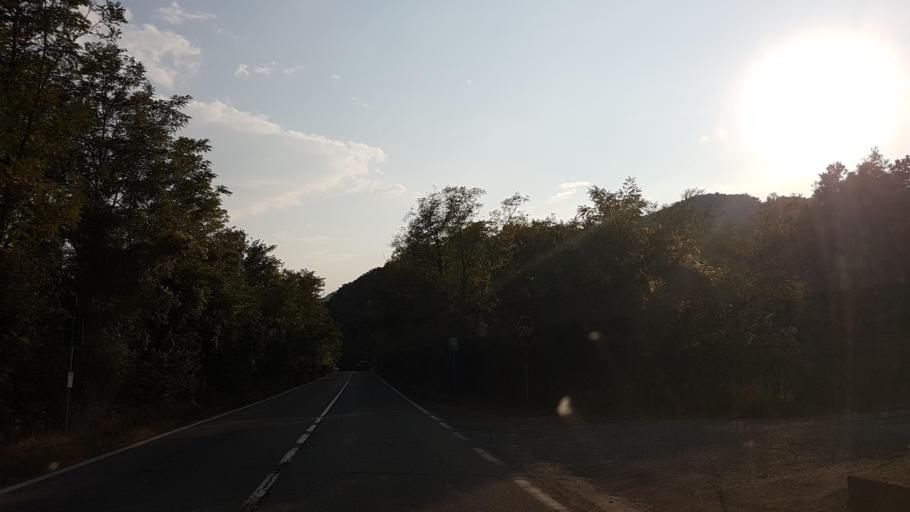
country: IT
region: Emilia-Romagna
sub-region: Provincia di Parma
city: Stazione Valmozzola
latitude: 44.5906
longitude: 9.9491
